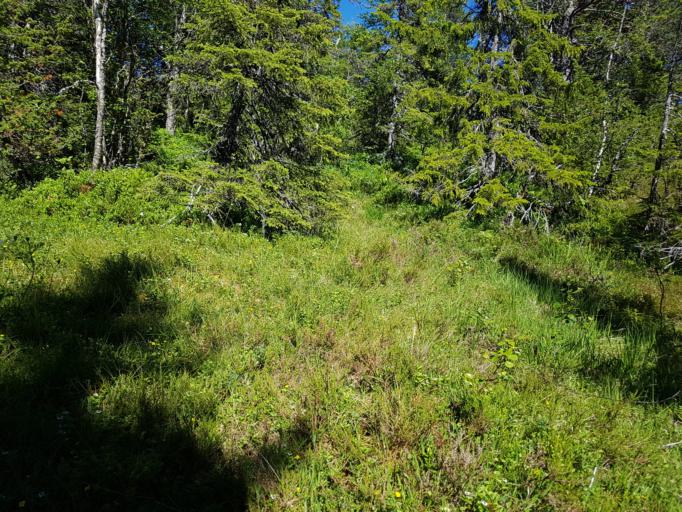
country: NO
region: Sor-Trondelag
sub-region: Melhus
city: Melhus
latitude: 63.4328
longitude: 10.2422
